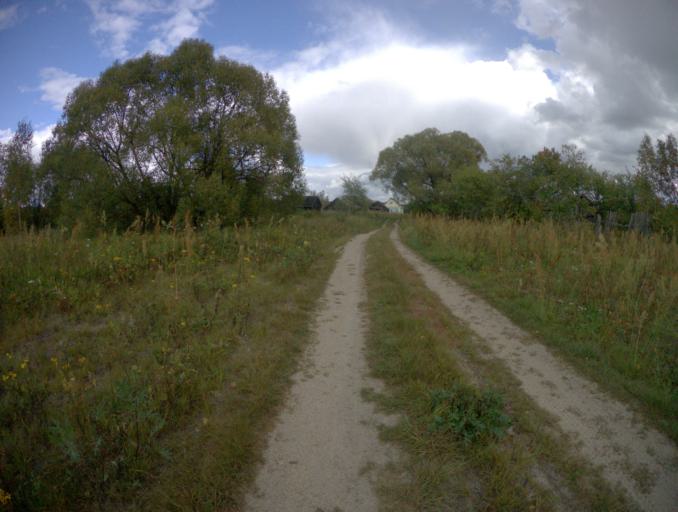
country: RU
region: Vladimir
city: Urshel'skiy
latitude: 55.7936
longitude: 40.1741
